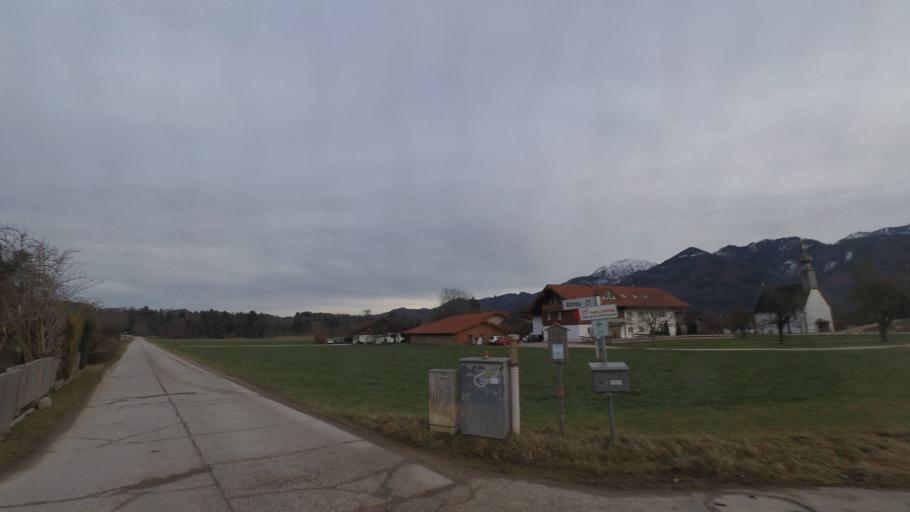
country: DE
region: Bavaria
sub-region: Upper Bavaria
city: Ubersee
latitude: 47.8074
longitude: 12.4955
